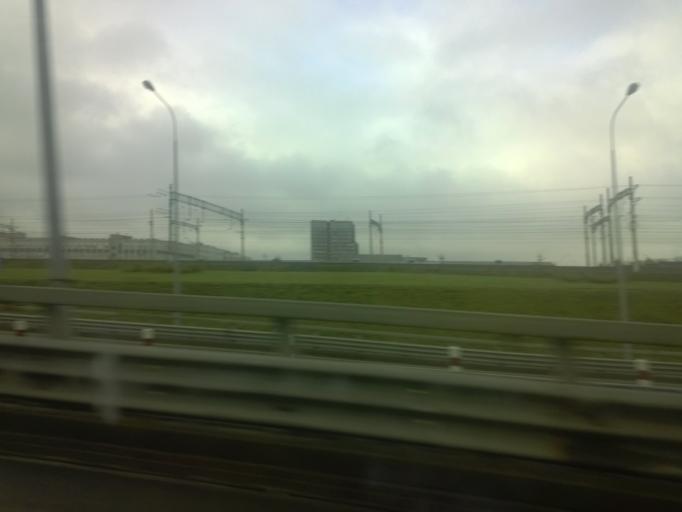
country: RU
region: St.-Petersburg
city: Avtovo
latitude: 59.8549
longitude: 30.2906
